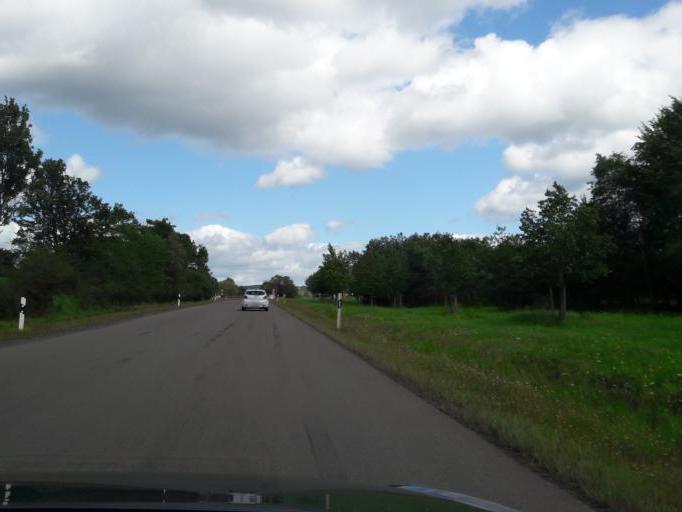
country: DE
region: Rheinland-Pfalz
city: Reichenbach
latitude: 49.6468
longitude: 7.2990
